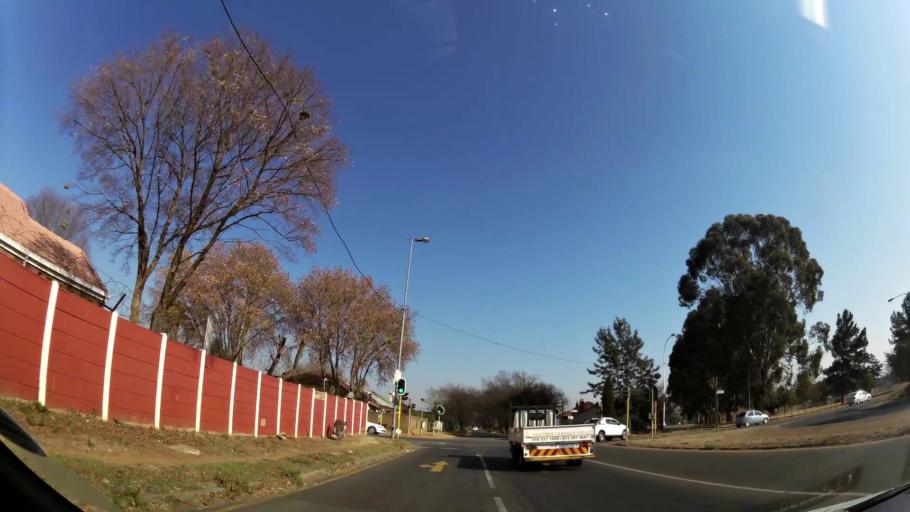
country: ZA
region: Gauteng
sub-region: Ekurhuleni Metropolitan Municipality
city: Boksburg
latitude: -26.2206
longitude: 28.2637
